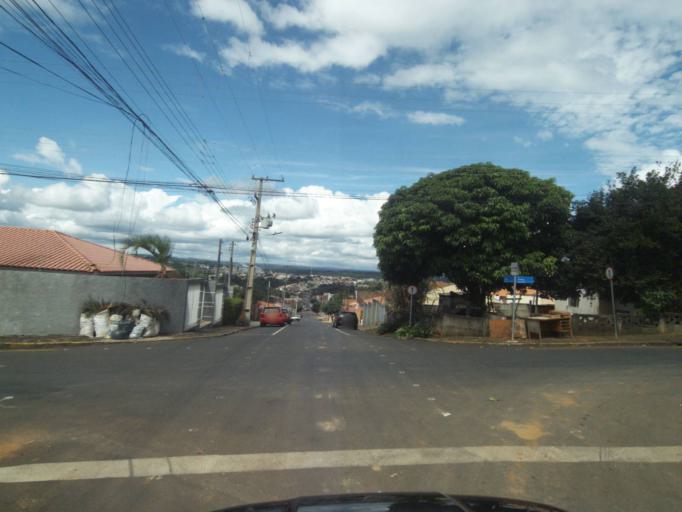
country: BR
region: Parana
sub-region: Telemaco Borba
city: Telemaco Borba
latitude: -24.3221
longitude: -50.6331
